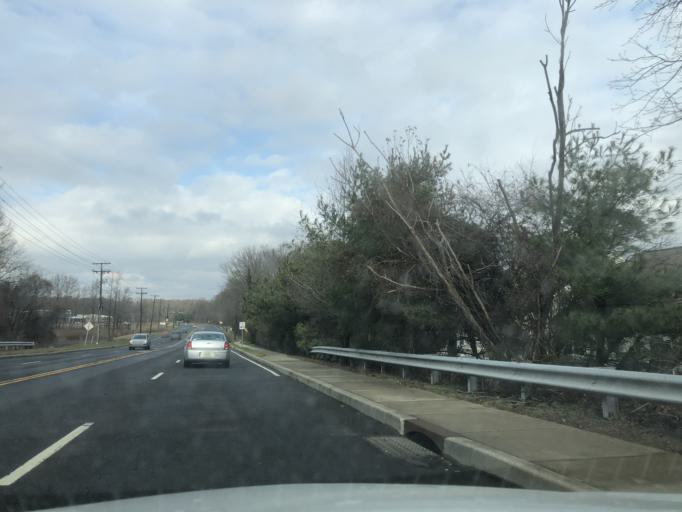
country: US
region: New Jersey
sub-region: Camden County
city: Glendora
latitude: 39.8373
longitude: -75.1017
